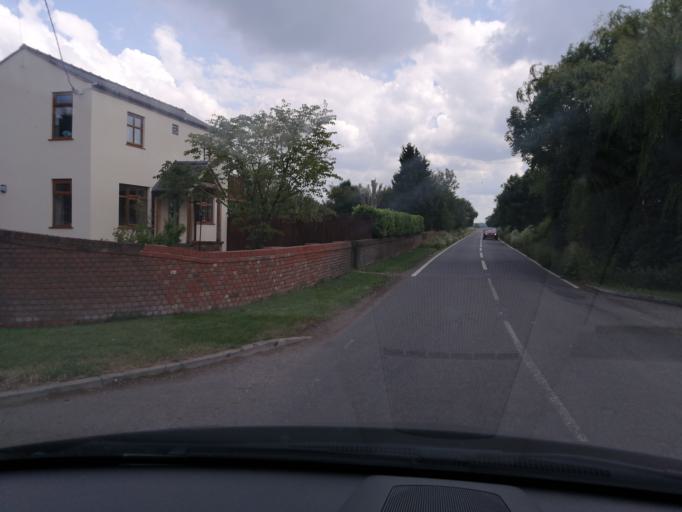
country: GB
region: England
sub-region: Cambridgeshire
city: Yaxley
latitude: 52.5087
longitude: -0.2595
